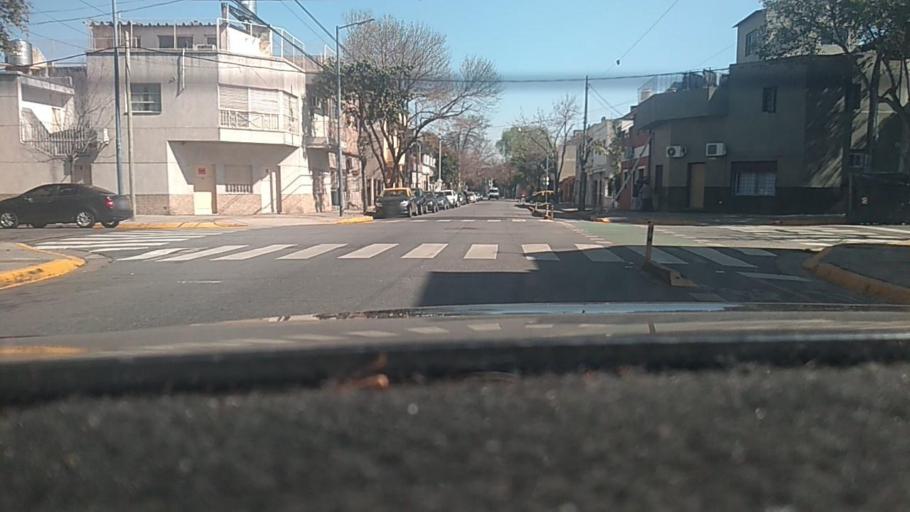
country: AR
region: Buenos Aires F.D.
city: Villa Santa Rita
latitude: -34.6168
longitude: -58.5106
